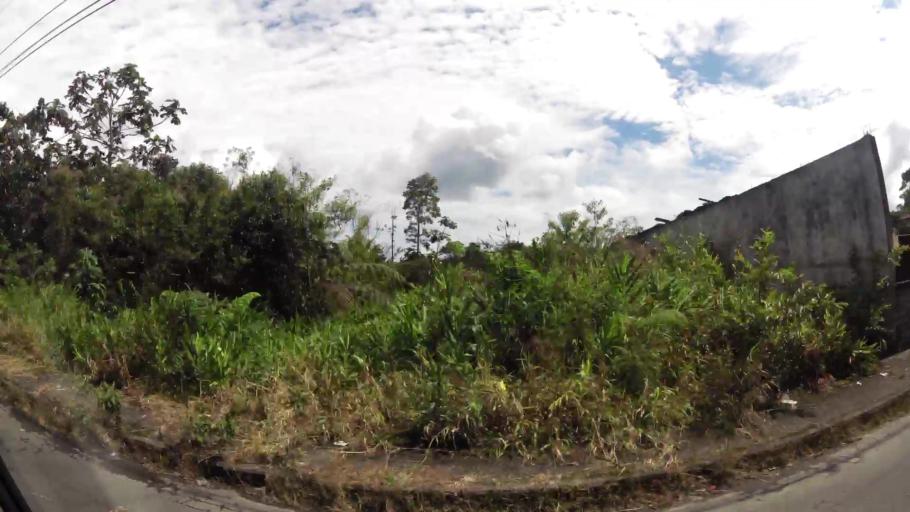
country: EC
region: Pastaza
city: Puyo
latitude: -1.4644
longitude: -78.1081
